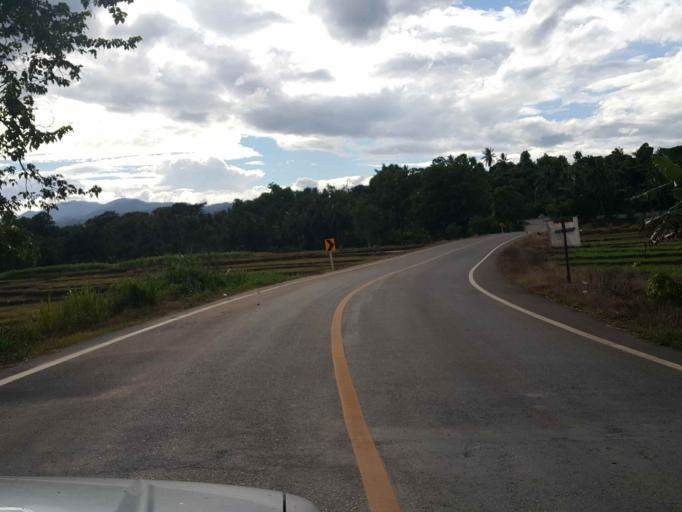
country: TH
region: Chiang Mai
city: Mae Chaem
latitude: 18.4802
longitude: 98.3816
